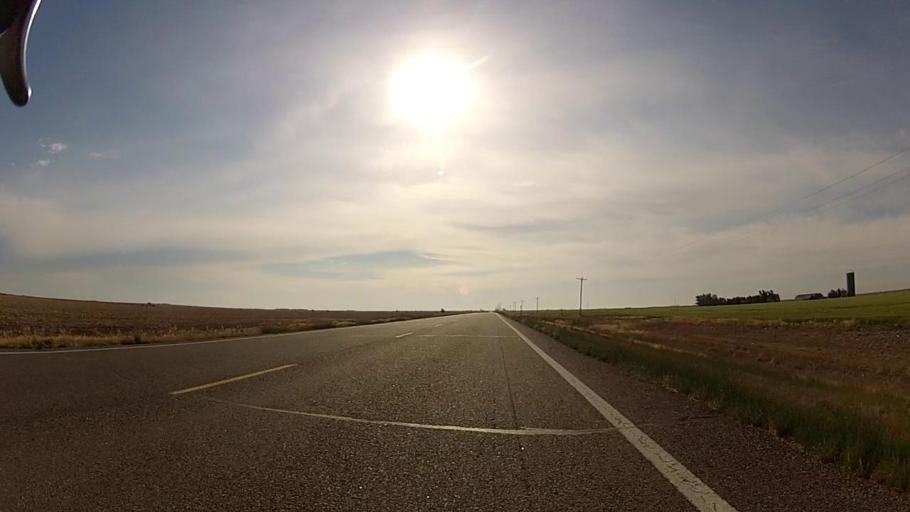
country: US
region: Kansas
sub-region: Grant County
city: Ulysses
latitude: 37.5766
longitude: -101.4489
